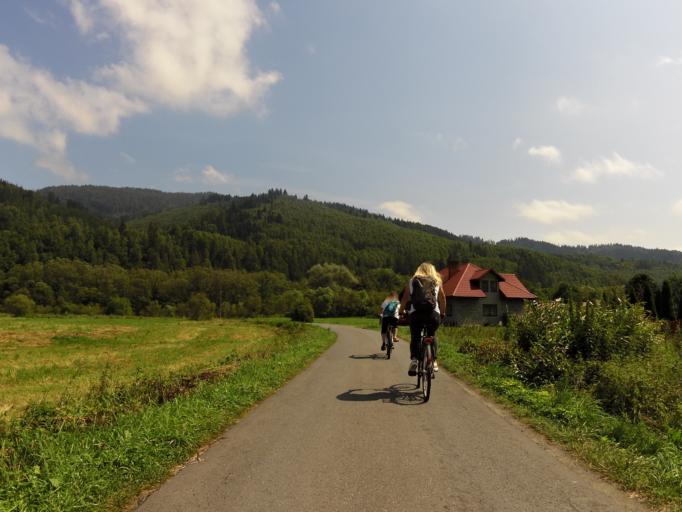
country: PL
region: Silesian Voivodeship
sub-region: Powiat zywiecki
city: Rajcza
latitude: 49.5223
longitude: 19.1095
